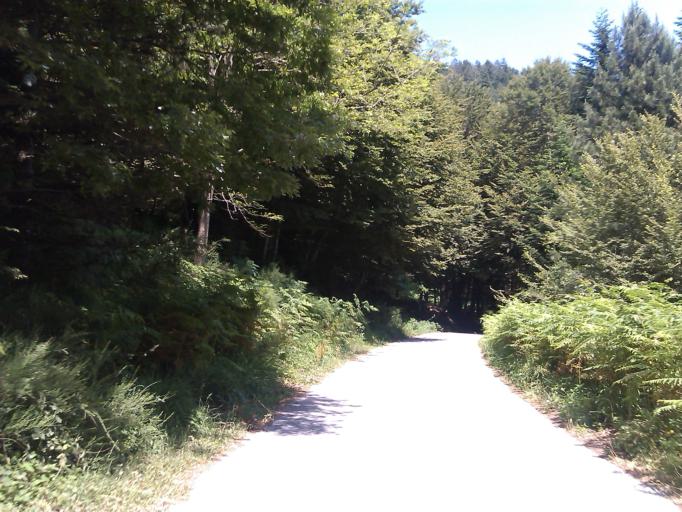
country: IT
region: Tuscany
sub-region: Provincia di Prato
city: Cantagallo
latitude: 43.9938
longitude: 11.0368
